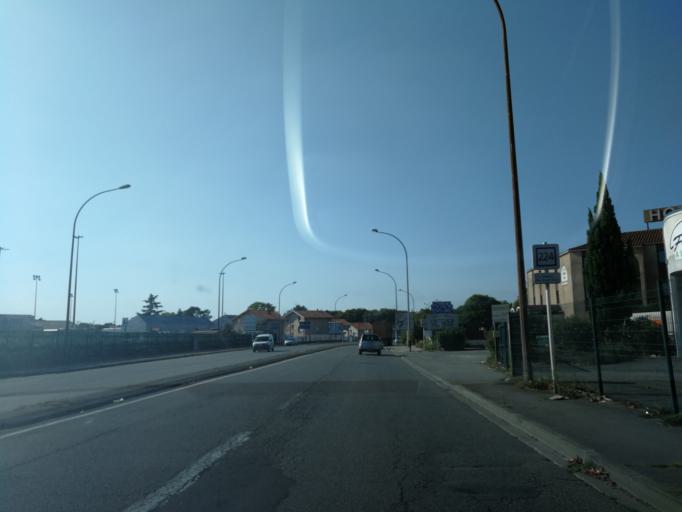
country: FR
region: Midi-Pyrenees
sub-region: Departement de la Haute-Garonne
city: Aucamville
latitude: 43.6454
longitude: 1.4270
